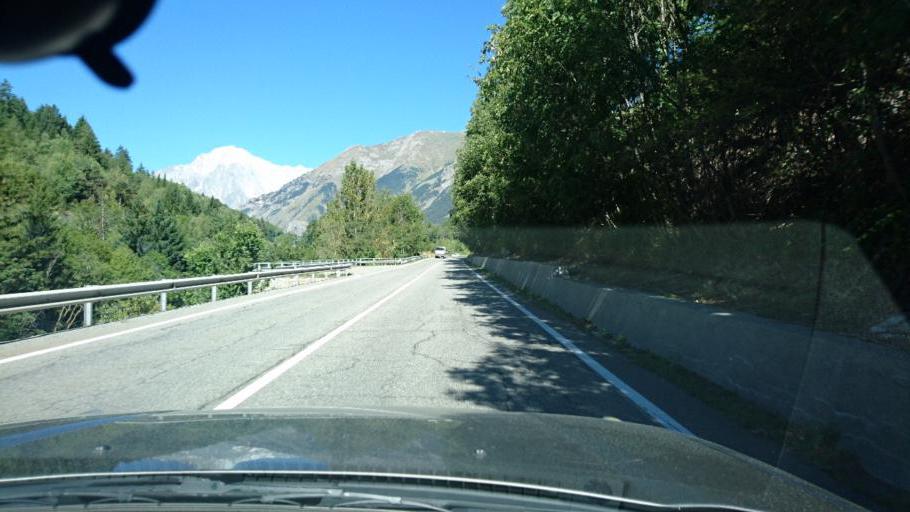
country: IT
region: Aosta Valley
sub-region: Valle d'Aosta
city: La Salle
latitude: 45.7374
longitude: 7.0703
